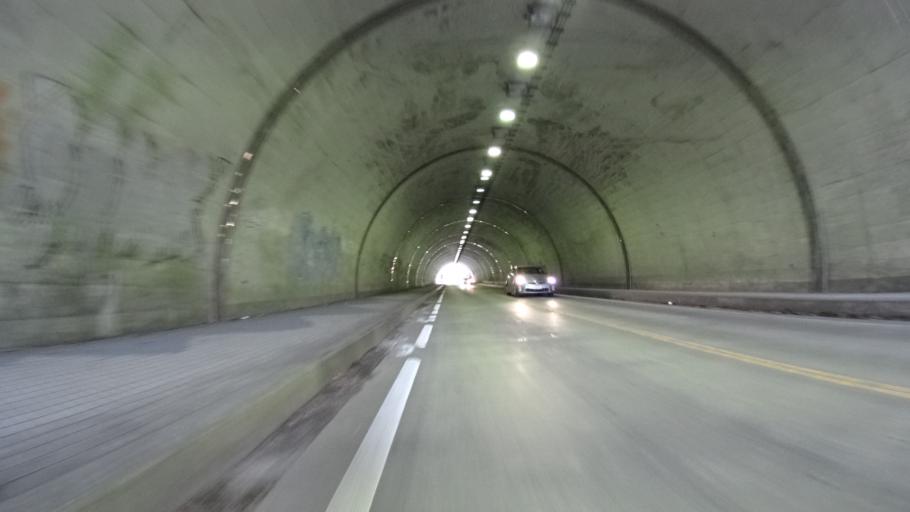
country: JP
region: Kanagawa
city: Zama
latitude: 35.5347
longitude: 139.2823
